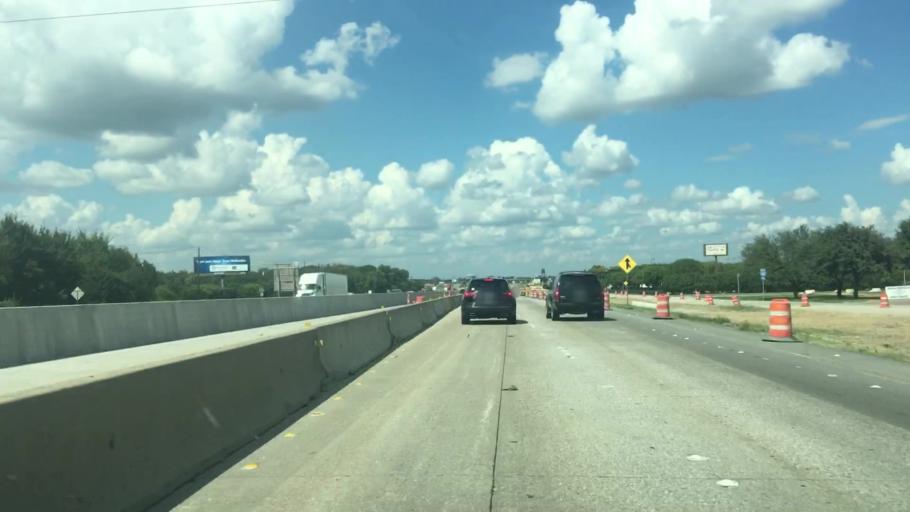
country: US
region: Texas
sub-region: Ellis County
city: Waxahachie
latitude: 32.4459
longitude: -96.8486
